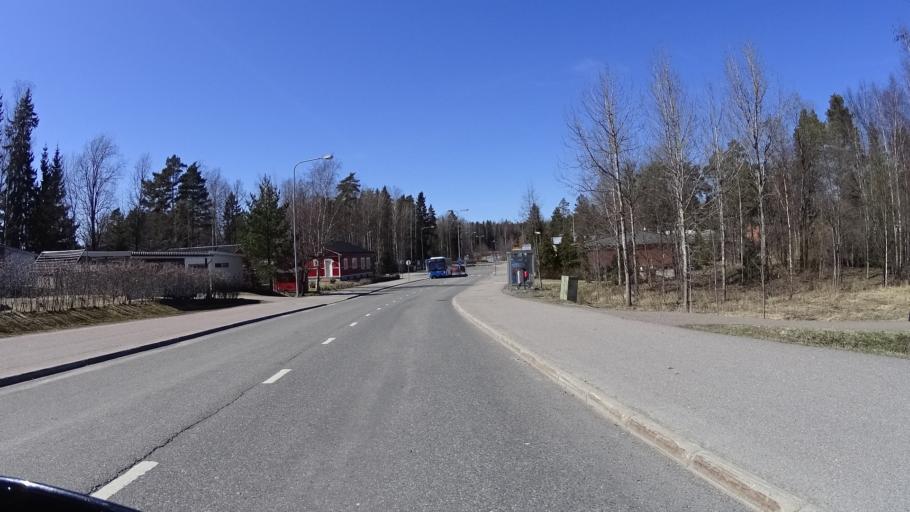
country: FI
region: Uusimaa
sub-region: Helsinki
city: Kilo
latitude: 60.2485
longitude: 24.8066
